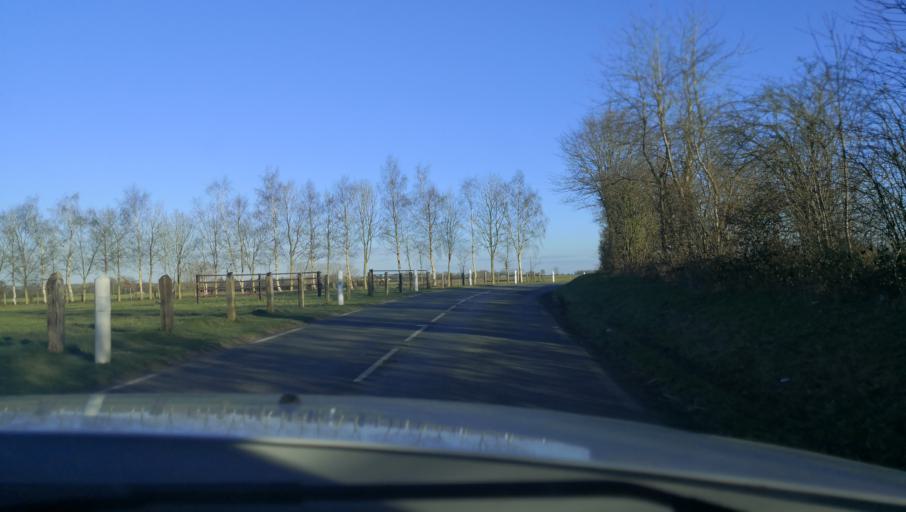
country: FR
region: Haute-Normandie
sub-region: Departement de la Seine-Maritime
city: Buchy
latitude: 49.6010
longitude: 1.3371
